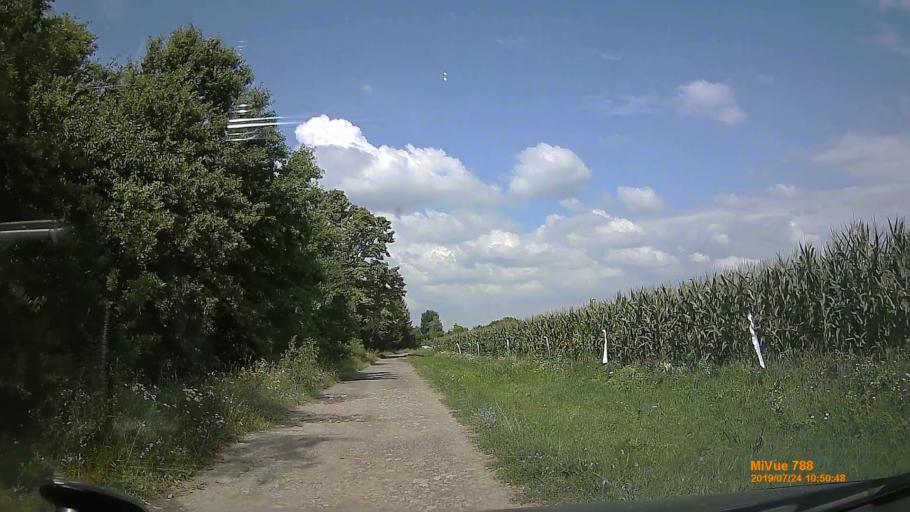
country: UA
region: Zakarpattia
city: Berehove
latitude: 48.1961
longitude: 22.5588
